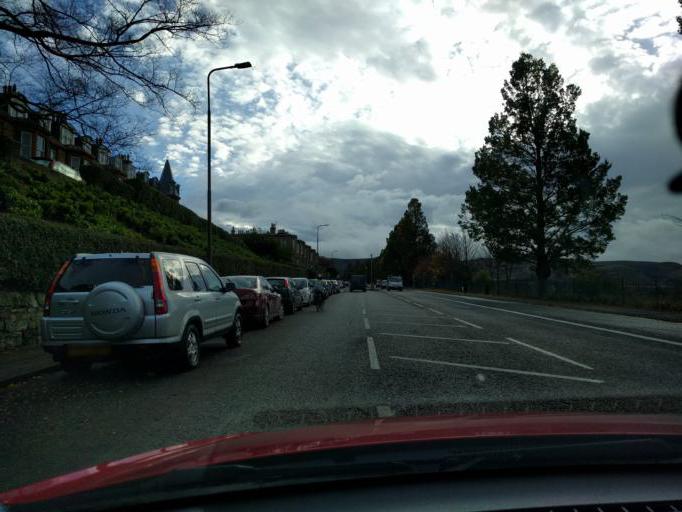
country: GB
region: Scotland
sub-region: Edinburgh
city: Edinburgh
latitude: 55.9166
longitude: -3.2133
